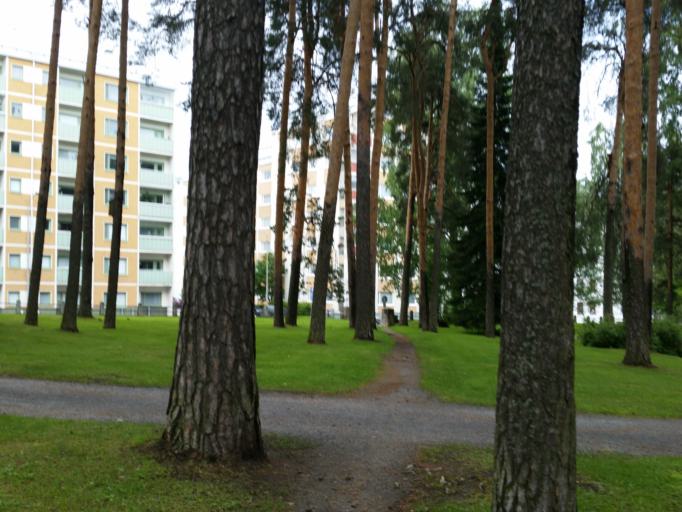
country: FI
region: Northern Savo
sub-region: Kuopio
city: Kuopio
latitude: 62.8941
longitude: 27.6731
